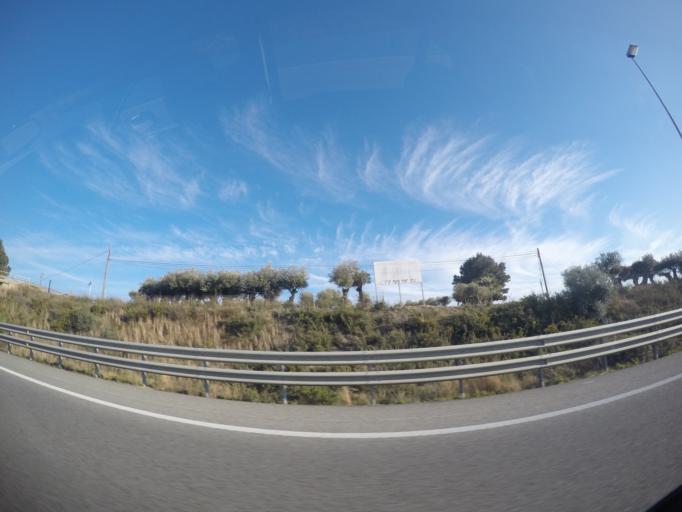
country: ES
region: Catalonia
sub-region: Provincia de Tarragona
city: Santa Oliva
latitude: 41.2695
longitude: 1.5508
